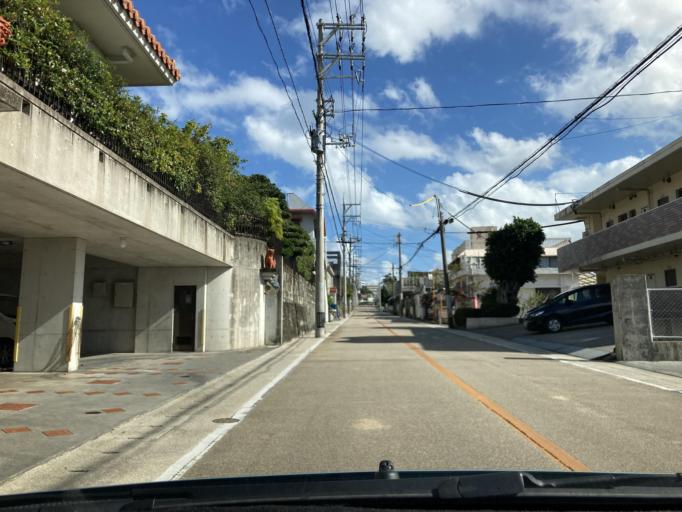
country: JP
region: Okinawa
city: Naha-shi
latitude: 26.2181
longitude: 127.7100
